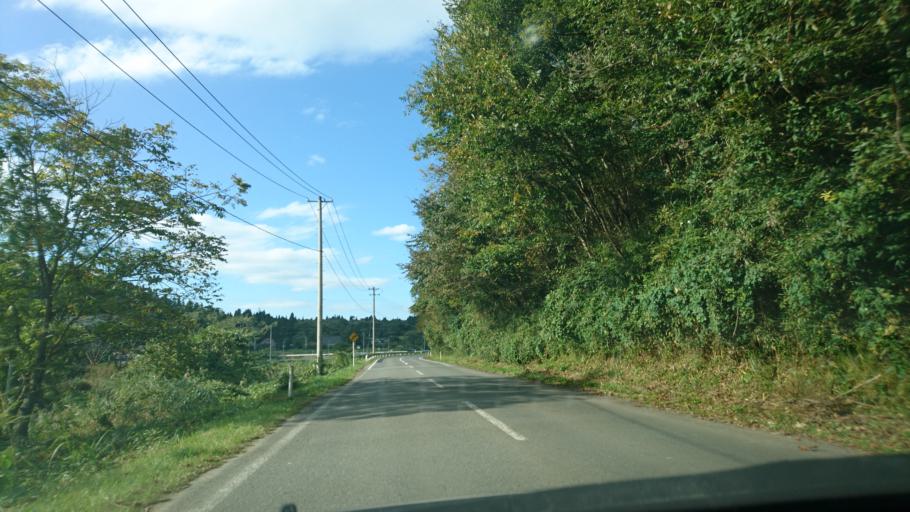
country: JP
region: Iwate
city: Ichinoseki
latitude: 38.8747
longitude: 141.3435
